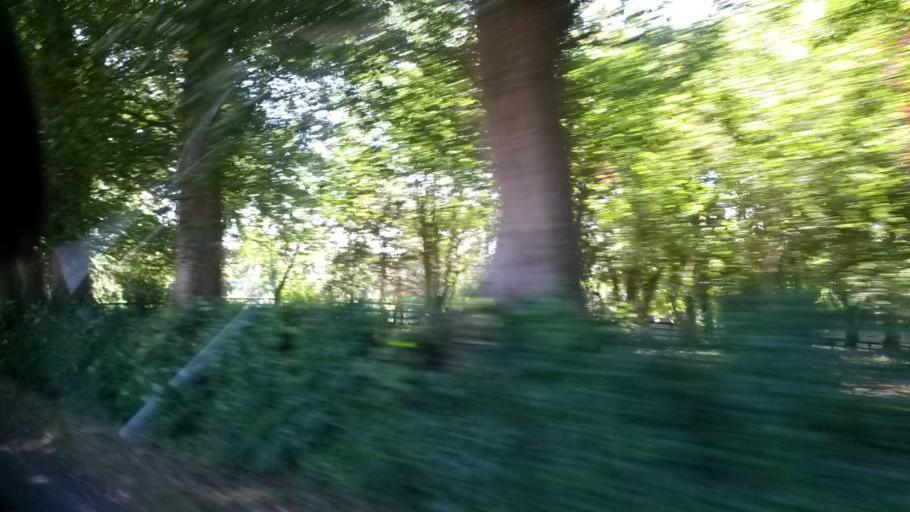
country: IE
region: Leinster
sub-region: An Mhi
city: Ashbourne
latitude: 53.5419
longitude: -6.3237
